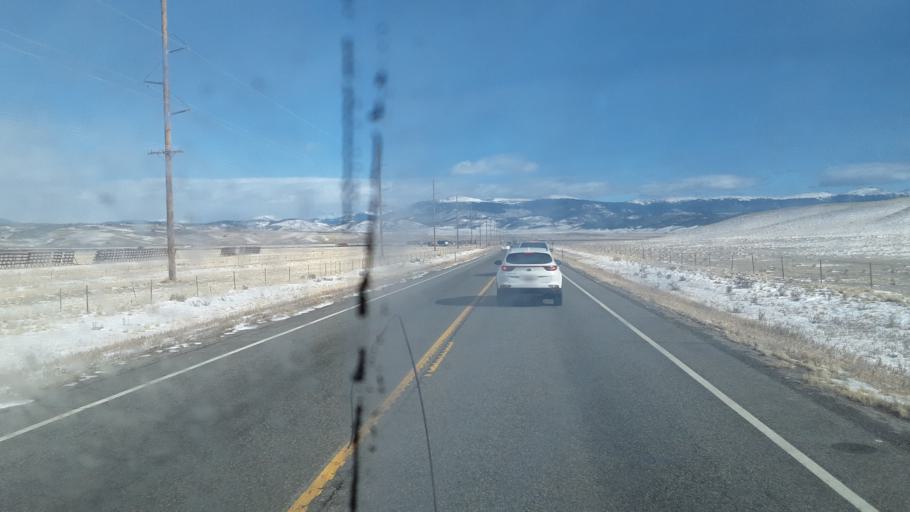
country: US
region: Colorado
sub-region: Park County
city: Fairplay
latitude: 39.3382
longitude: -105.8571
